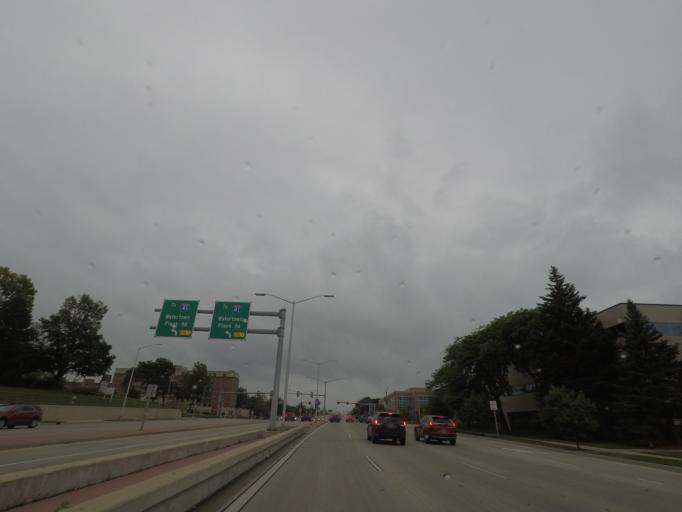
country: US
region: Wisconsin
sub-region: Waukesha County
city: Elm Grove
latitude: 43.0466
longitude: -88.0473
